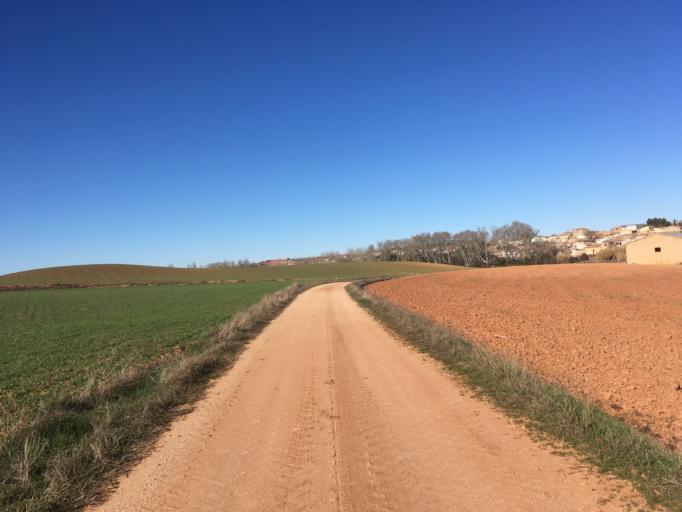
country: ES
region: Castille-La Mancha
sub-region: Provincia de Cuenca
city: Atalaya del Canavate
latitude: 39.5442
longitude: -2.2461
